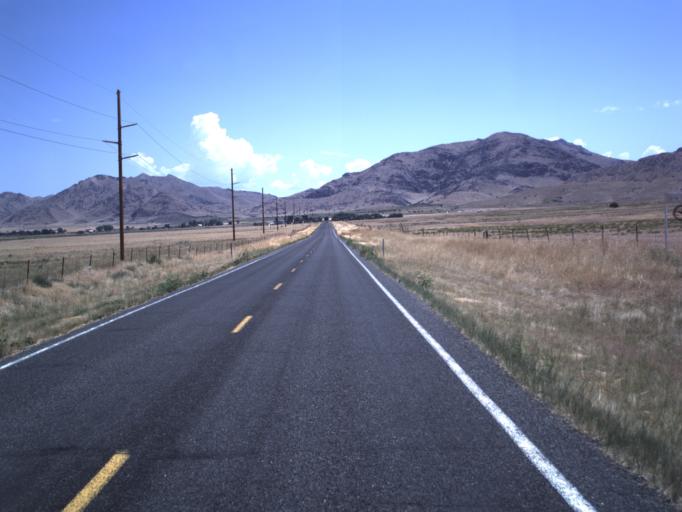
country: US
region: Utah
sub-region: Millard County
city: Delta
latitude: 39.4568
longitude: -112.2977
